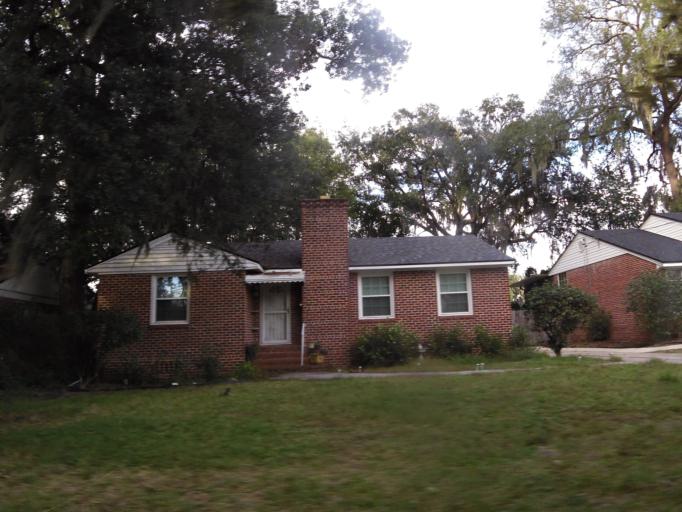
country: US
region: Florida
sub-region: Duval County
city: Jacksonville
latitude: 30.3897
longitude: -81.6606
